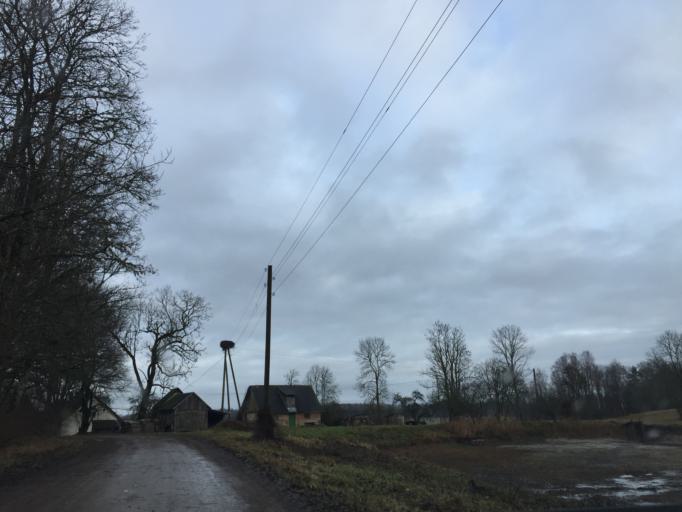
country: LV
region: Vainode
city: Vainode
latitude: 56.6145
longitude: 21.7951
